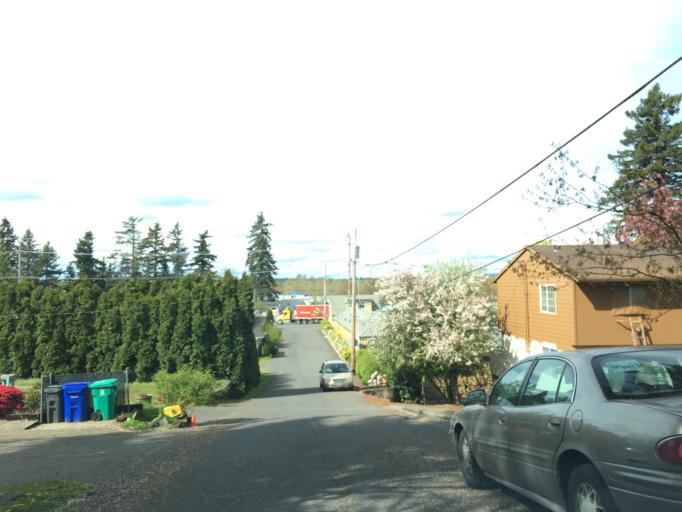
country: US
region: Oregon
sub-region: Multnomah County
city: Lents
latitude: 45.5563
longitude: -122.5399
